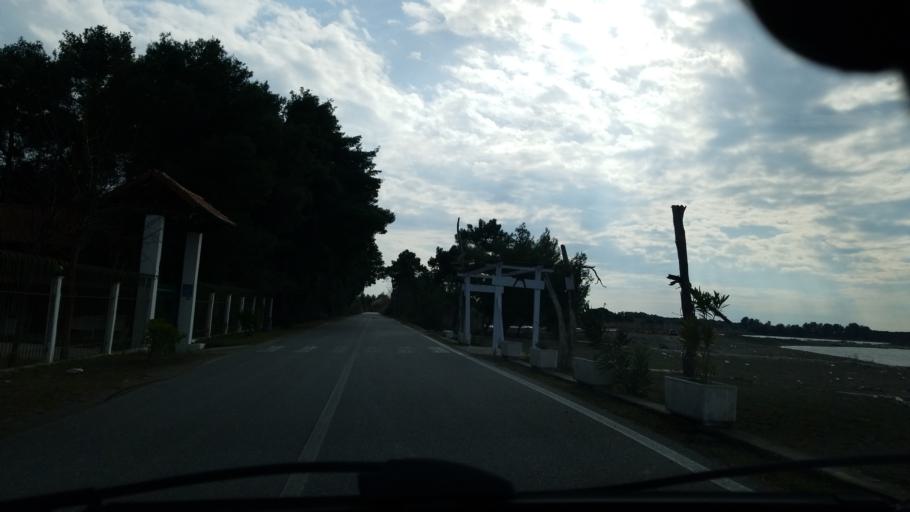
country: AL
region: Lezhe
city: Shengjin
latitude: 41.7680
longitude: 19.5988
